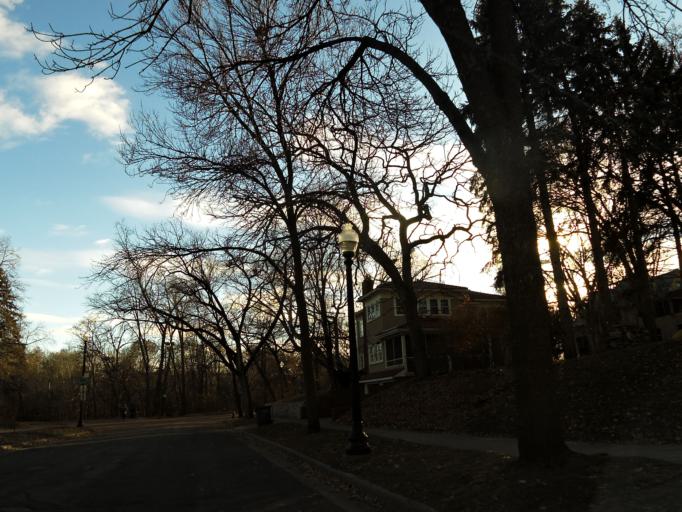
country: US
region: Minnesota
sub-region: Hennepin County
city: Richfield
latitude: 44.9112
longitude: -93.2729
